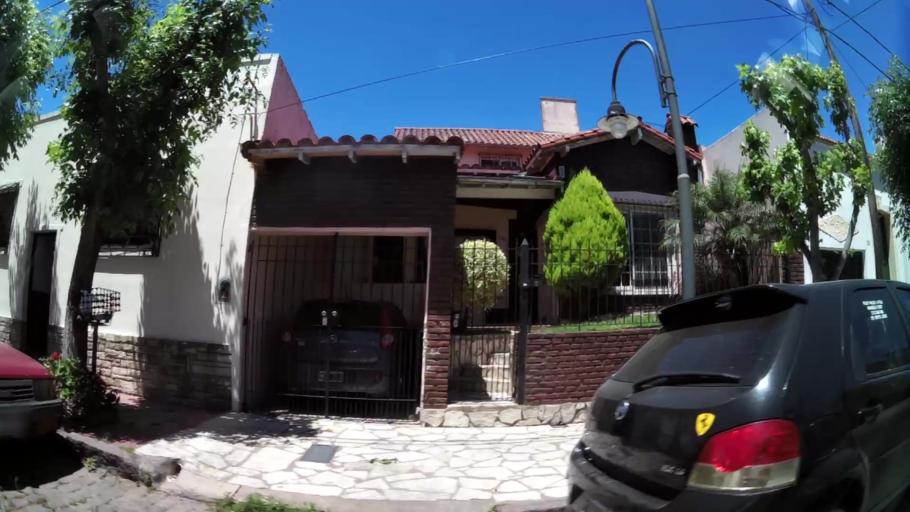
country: AR
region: Buenos Aires
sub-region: Partido de Tigre
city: Tigre
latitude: -34.4465
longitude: -58.5552
